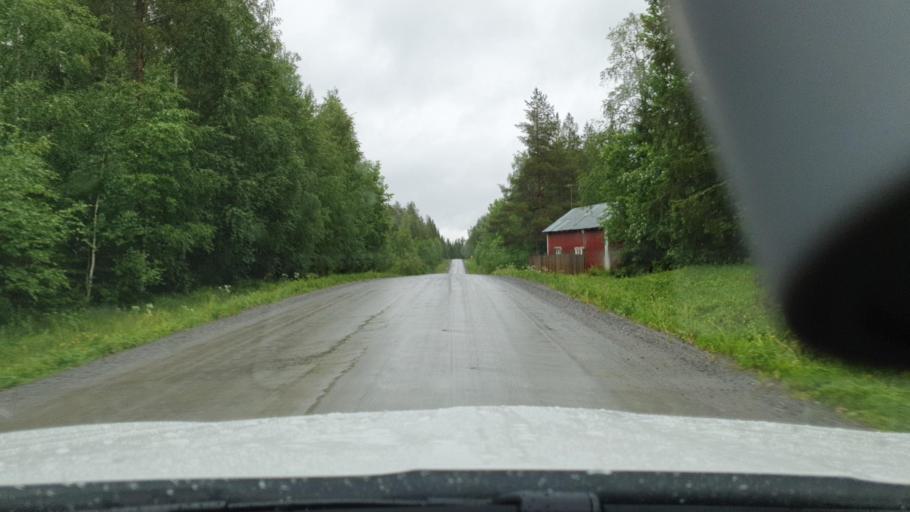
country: SE
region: Vaesterbotten
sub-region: Skelleftea Kommun
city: Burtraesk
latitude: 64.3687
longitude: 20.3903
